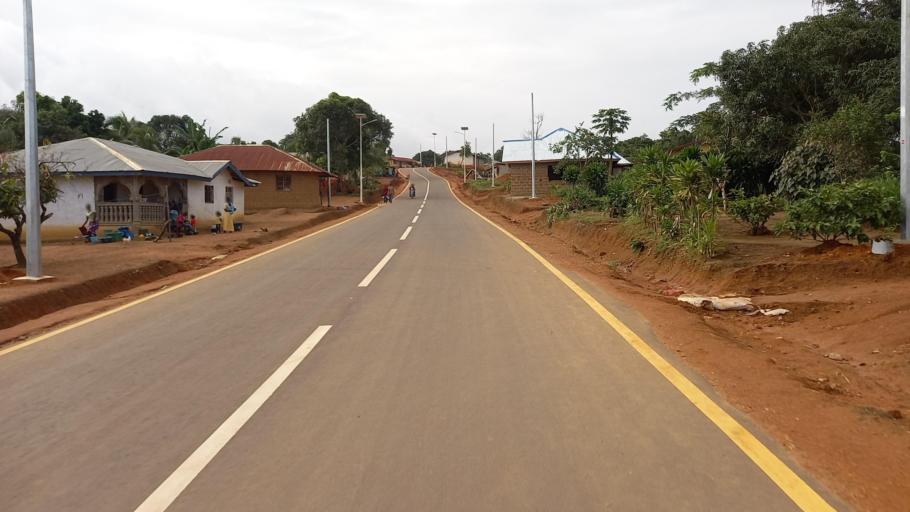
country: SL
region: Eastern Province
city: Kailahun
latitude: 8.2729
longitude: -10.5796
